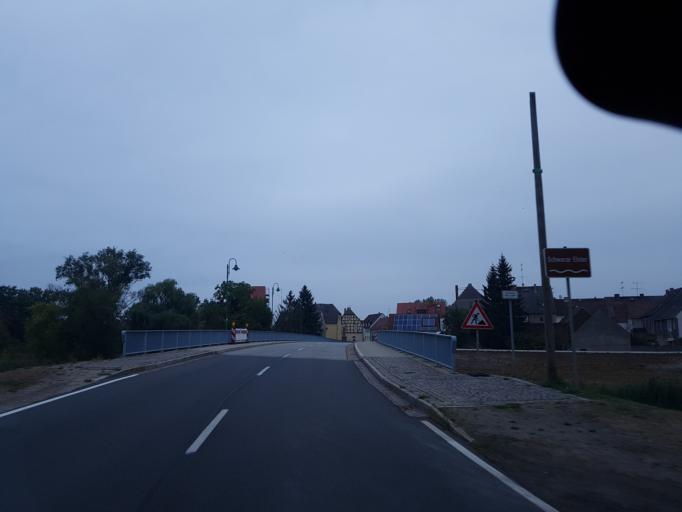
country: DE
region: Saxony-Anhalt
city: Annaburg
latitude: 51.7916
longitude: 13.0246
